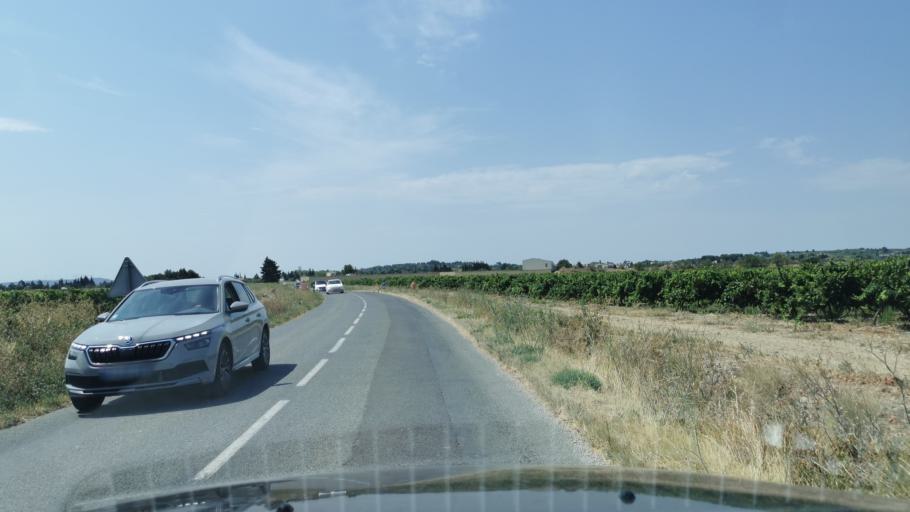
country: FR
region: Languedoc-Roussillon
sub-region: Departement de l'Aude
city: Ginestas
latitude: 43.2799
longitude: 2.8884
